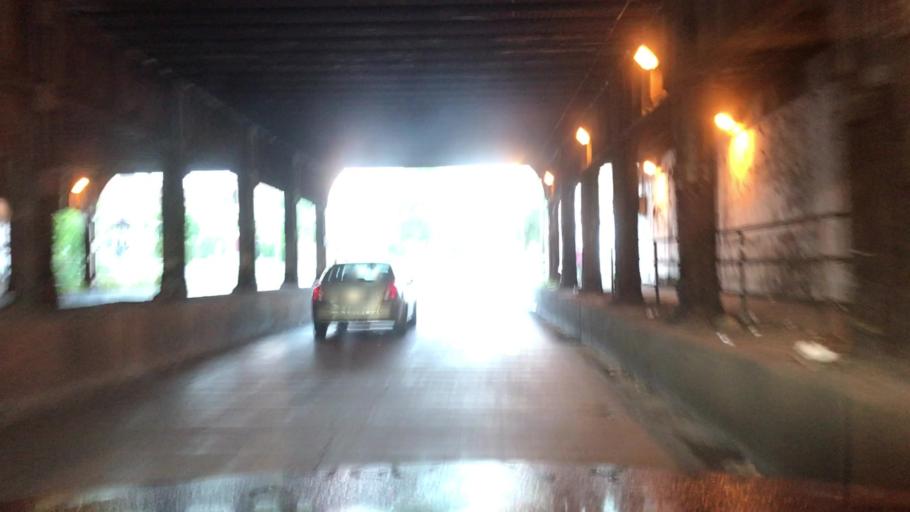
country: US
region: Illinois
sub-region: Cook County
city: Chicago
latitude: 41.8887
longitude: -87.6672
